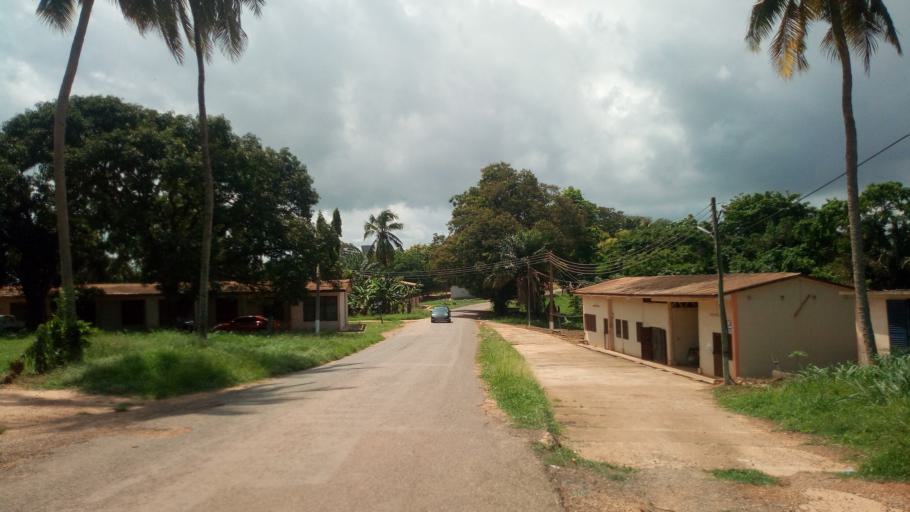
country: GH
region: Western
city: Sekondi-Takoradi
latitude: 4.9301
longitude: -1.7461
